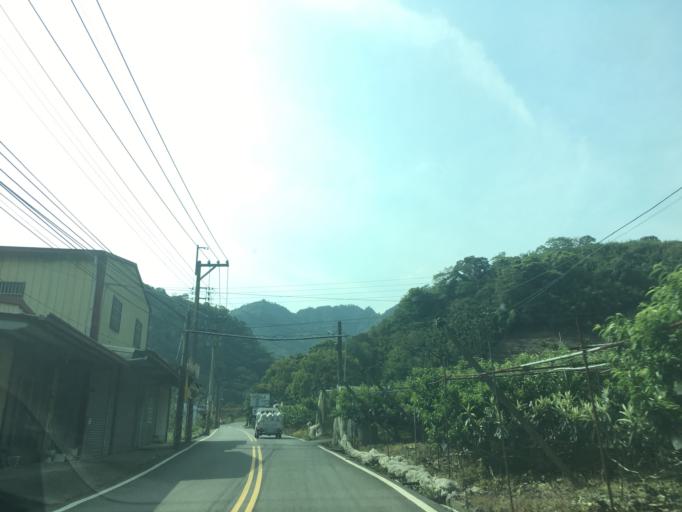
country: TW
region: Taiwan
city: Fengyuan
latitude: 24.1646
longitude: 120.8251
